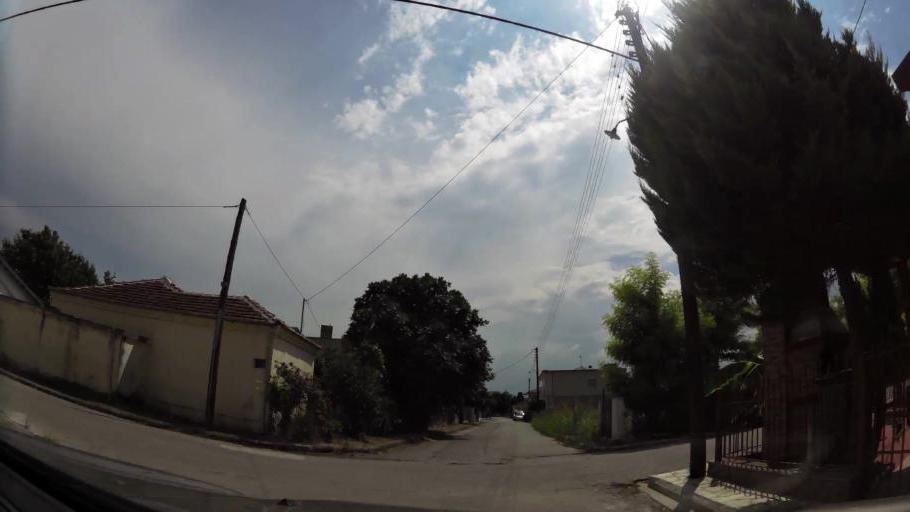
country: GR
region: Central Macedonia
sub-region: Nomos Pierias
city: Korinos
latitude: 40.3180
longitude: 22.5886
